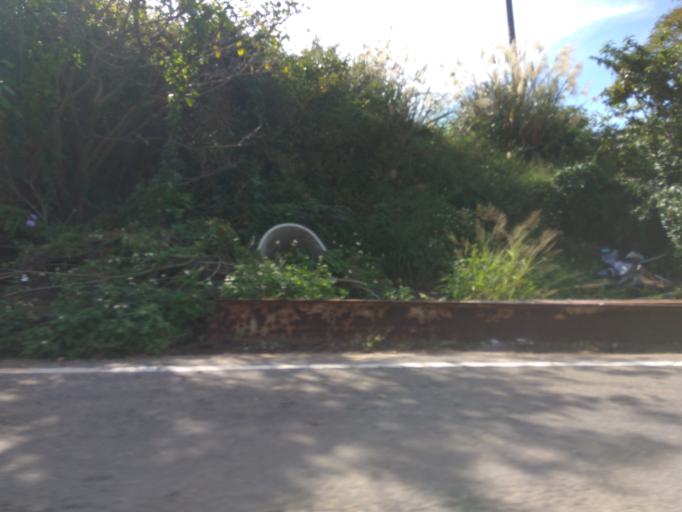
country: TW
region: Taiwan
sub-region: Hsinchu
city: Zhubei
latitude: 25.0112
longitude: 121.0791
